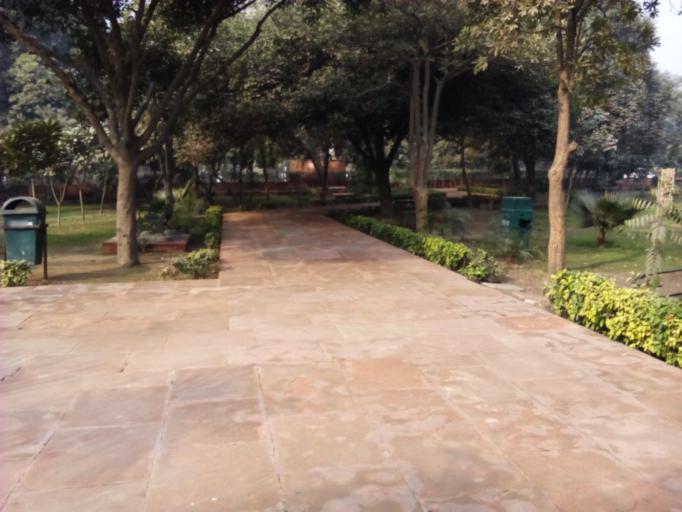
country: IN
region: Uttar Pradesh
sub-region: Gautam Buddha Nagar
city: Noida
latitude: 28.6445
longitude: 77.3209
